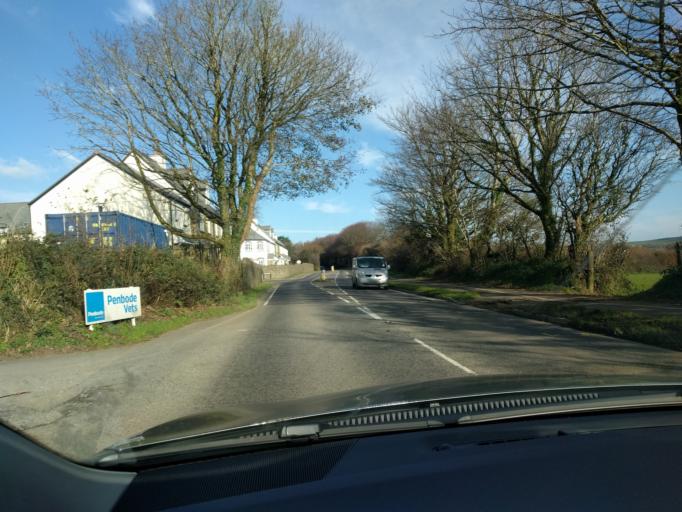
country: GB
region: England
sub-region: Cornwall
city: Camelford
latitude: 50.6151
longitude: -4.6850
